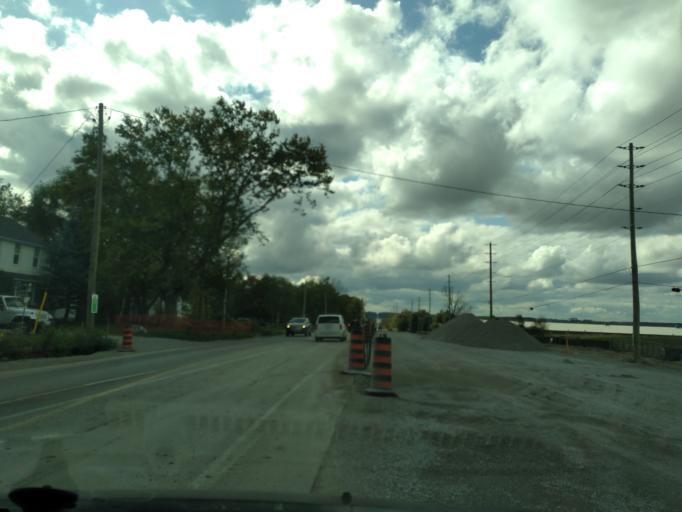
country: CA
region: Ontario
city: Innisfil
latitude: 44.2996
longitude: -79.6145
